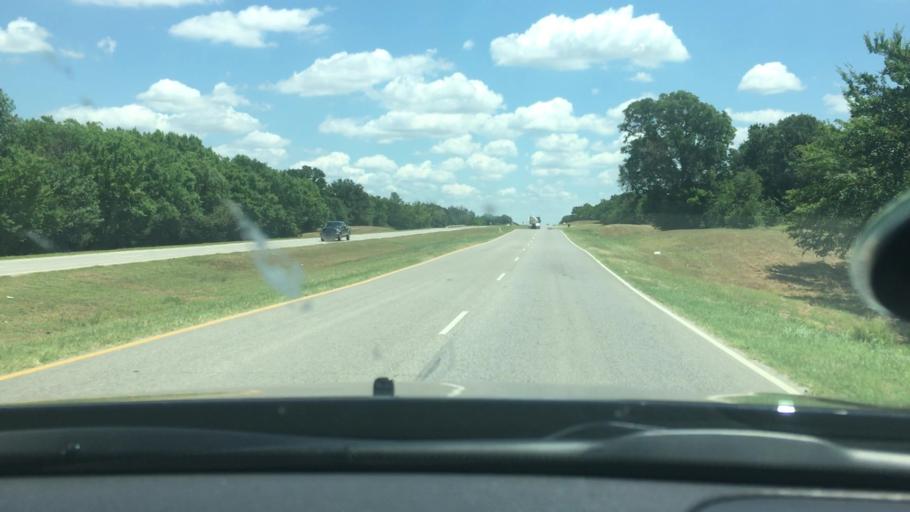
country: US
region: Oklahoma
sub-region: Carter County
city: Wilson
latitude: 34.1728
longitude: -97.3992
